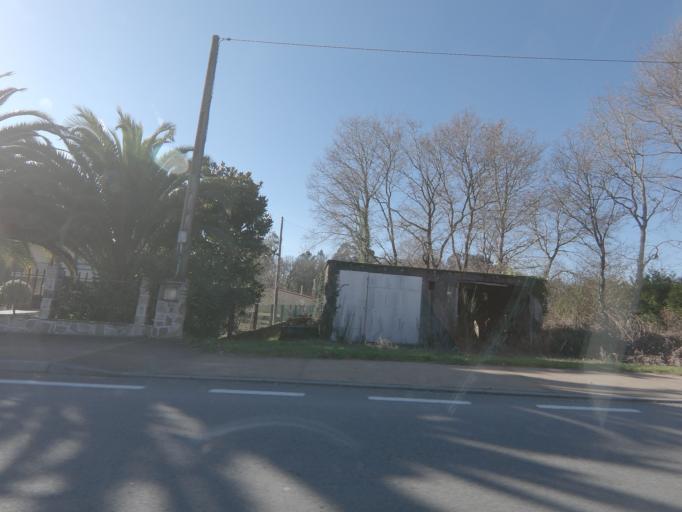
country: ES
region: Galicia
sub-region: Provincia da Coruna
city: Ribeira
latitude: 42.7130
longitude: -8.4460
